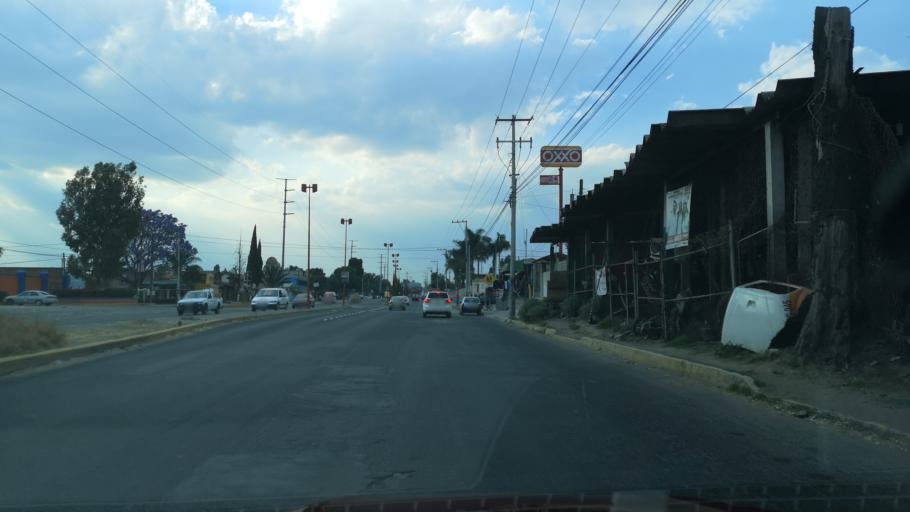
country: MX
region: Puebla
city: Cuanala
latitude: 19.0942
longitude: -98.3395
